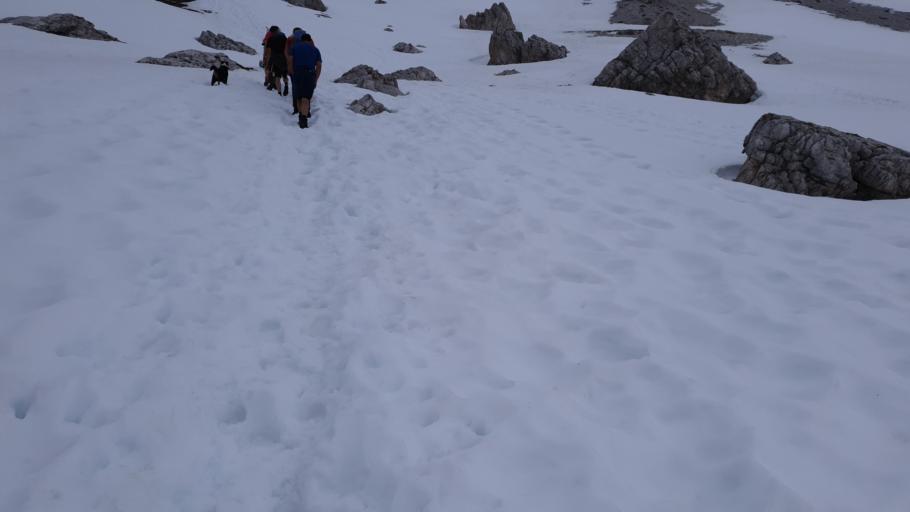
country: IT
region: Trentino-Alto Adige
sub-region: Bolzano
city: Sesto
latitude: 46.6218
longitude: 12.3131
